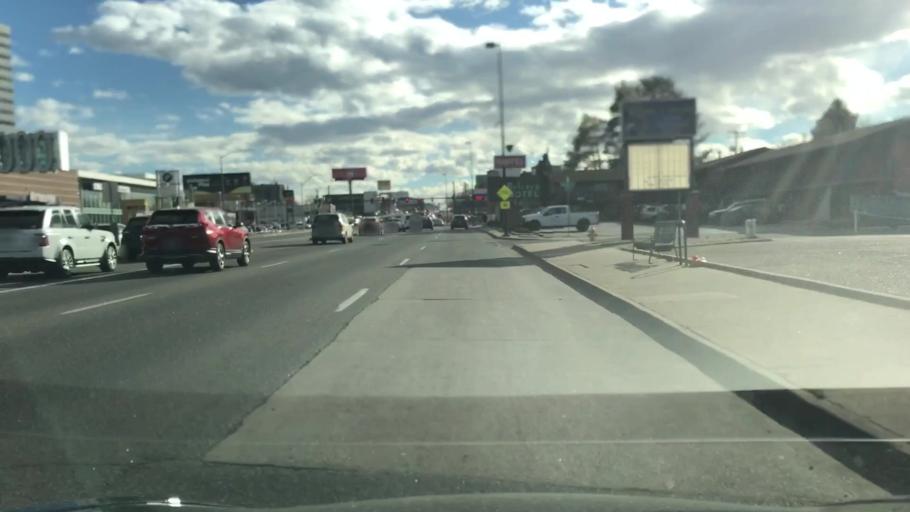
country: US
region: Colorado
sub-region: Arapahoe County
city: Glendale
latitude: 39.6987
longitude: -104.9409
